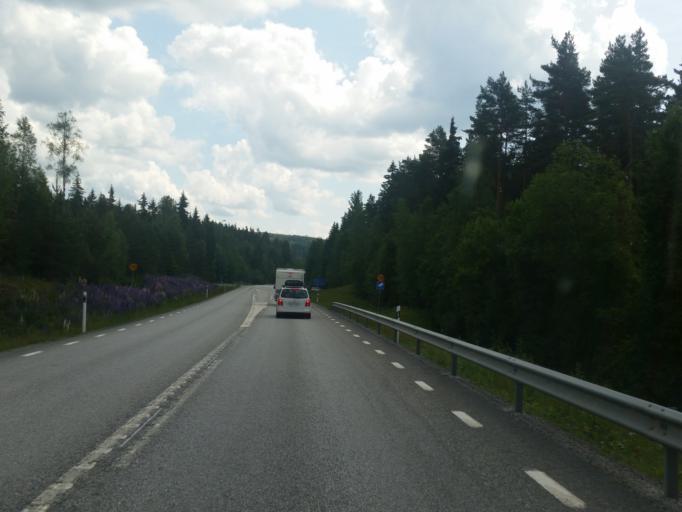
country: SE
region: OErebro
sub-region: Ljusnarsbergs Kommun
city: Kopparberg
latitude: 59.8714
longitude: 15.0440
